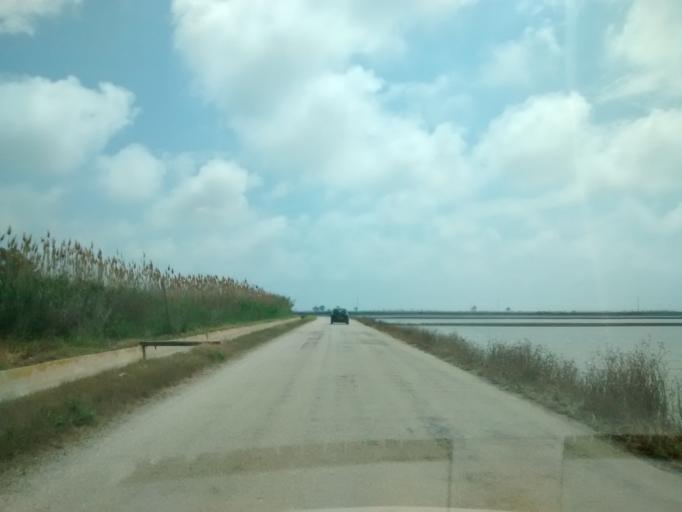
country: ES
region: Catalonia
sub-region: Provincia de Tarragona
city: Deltebre
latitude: 40.7009
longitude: 0.8261
